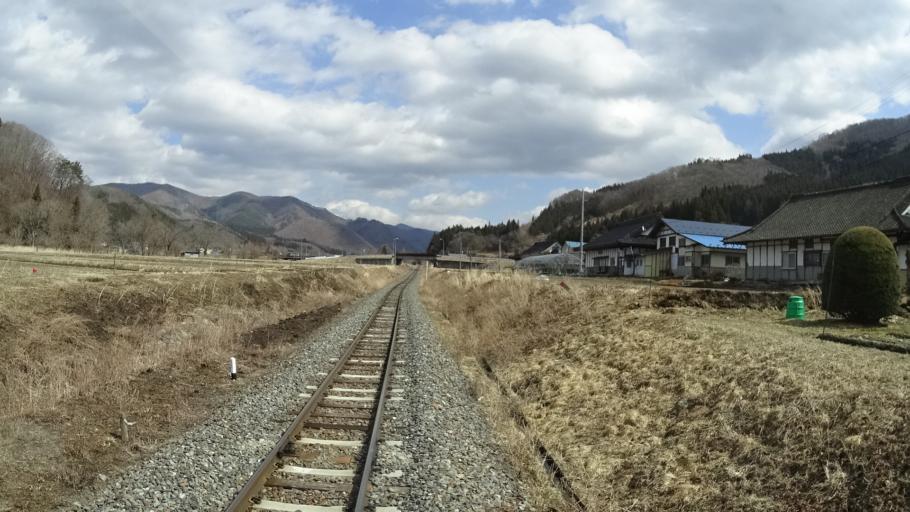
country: JP
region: Iwate
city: Tono
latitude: 39.2645
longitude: 141.5970
